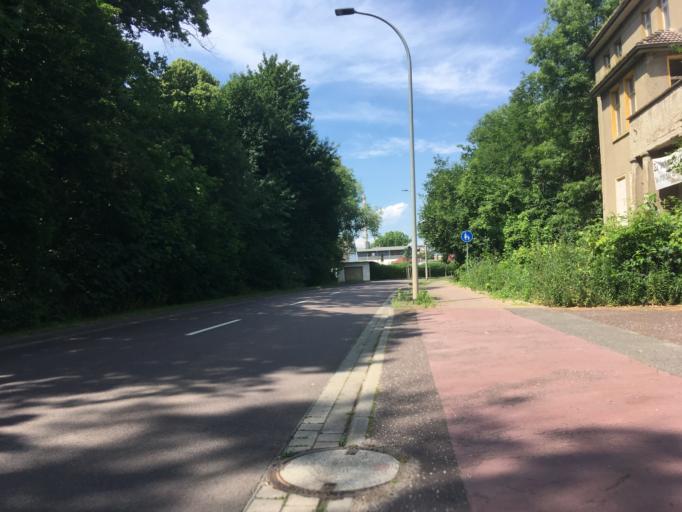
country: DE
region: Saxony-Anhalt
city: Koethen
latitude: 51.7527
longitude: 12.0107
